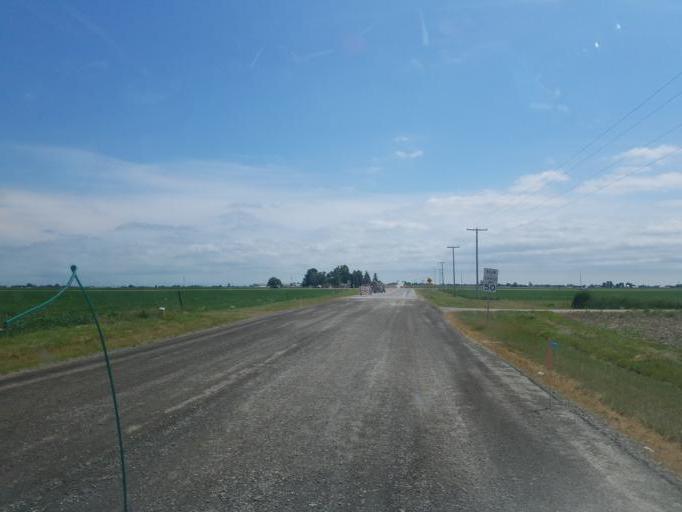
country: US
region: Indiana
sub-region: Allen County
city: Woodburn
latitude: 41.1573
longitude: -84.8488
